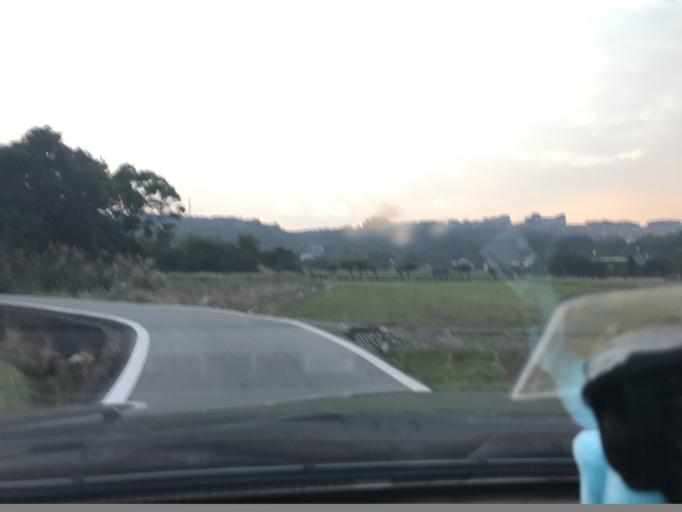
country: TW
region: Taiwan
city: Daxi
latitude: 24.8549
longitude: 121.2114
